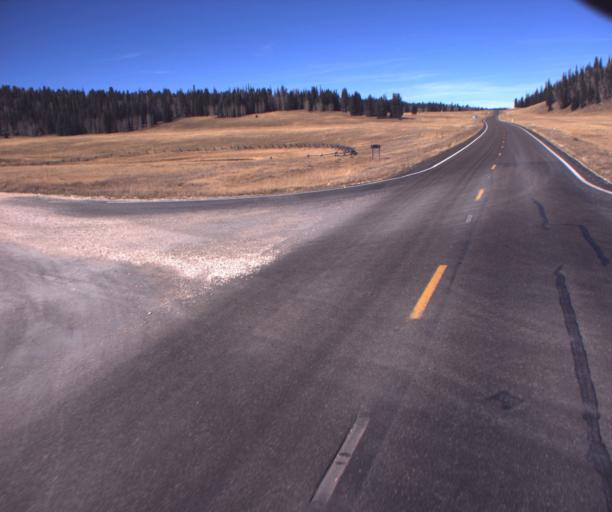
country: US
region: Arizona
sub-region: Coconino County
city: Grand Canyon
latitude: 36.4011
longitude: -112.1294
